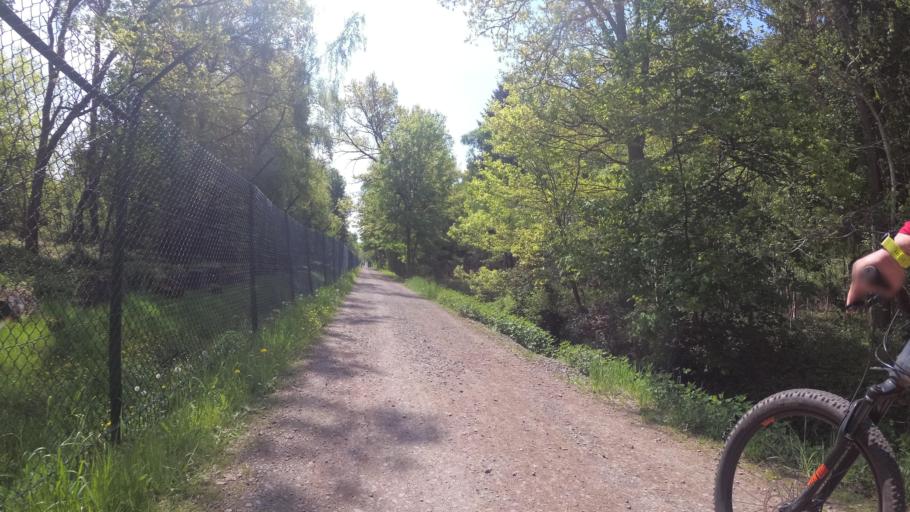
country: DE
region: Rheinland-Pfalz
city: Landstuhl
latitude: 49.4281
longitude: 7.5687
